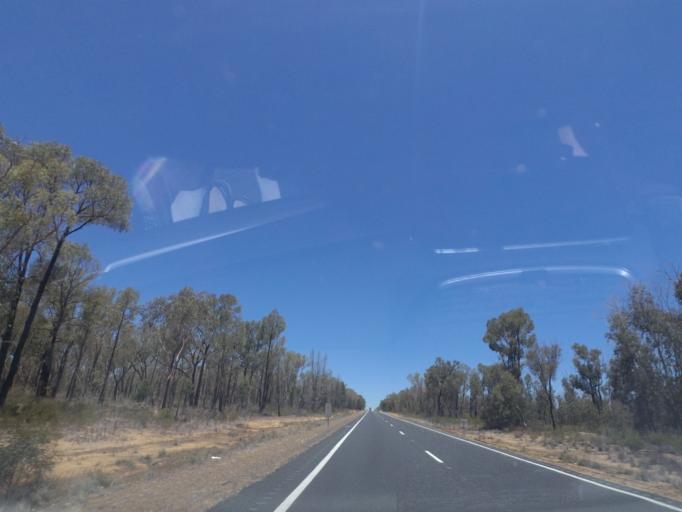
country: AU
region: New South Wales
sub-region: Warrumbungle Shire
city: Coonabarabran
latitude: -30.9581
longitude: 149.4202
